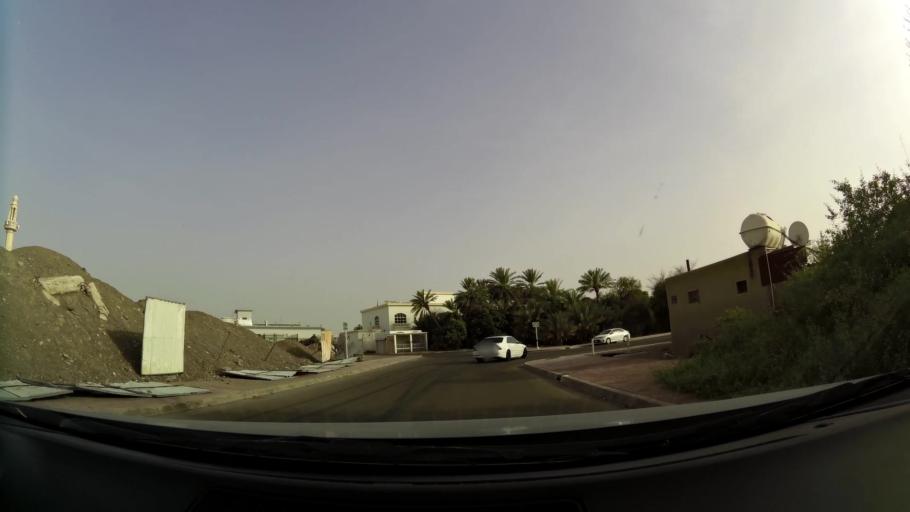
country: AE
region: Abu Dhabi
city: Al Ain
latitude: 24.2186
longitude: 55.7052
